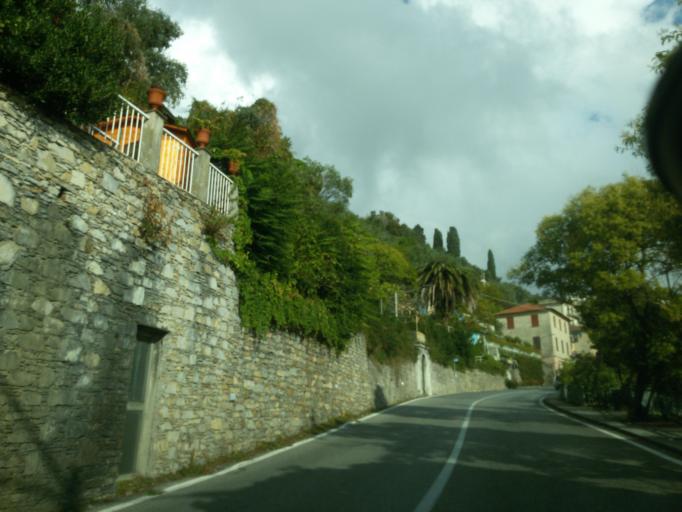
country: IT
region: Liguria
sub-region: Provincia di Genova
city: Camogli
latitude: 44.3485
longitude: 9.1641
